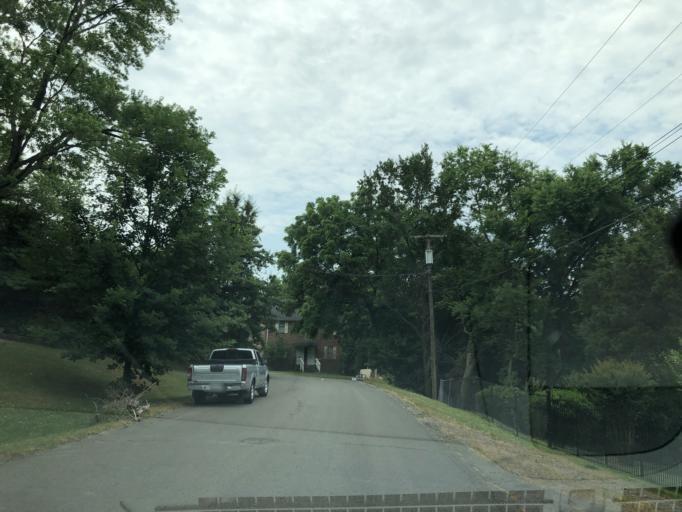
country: US
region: Tennessee
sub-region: Rutherford County
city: La Vergne
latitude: 36.0670
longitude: -86.6757
